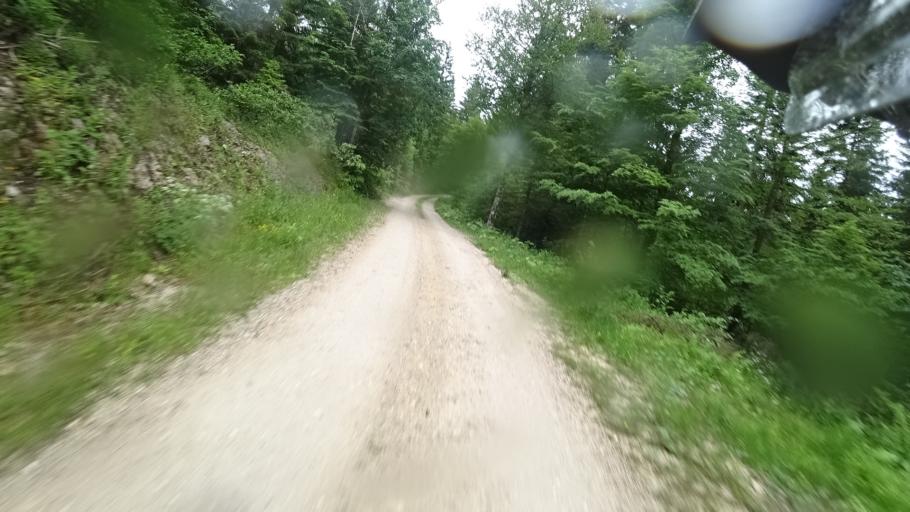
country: HR
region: Primorsko-Goranska
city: Vrbovsko
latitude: 45.3027
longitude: 14.9502
